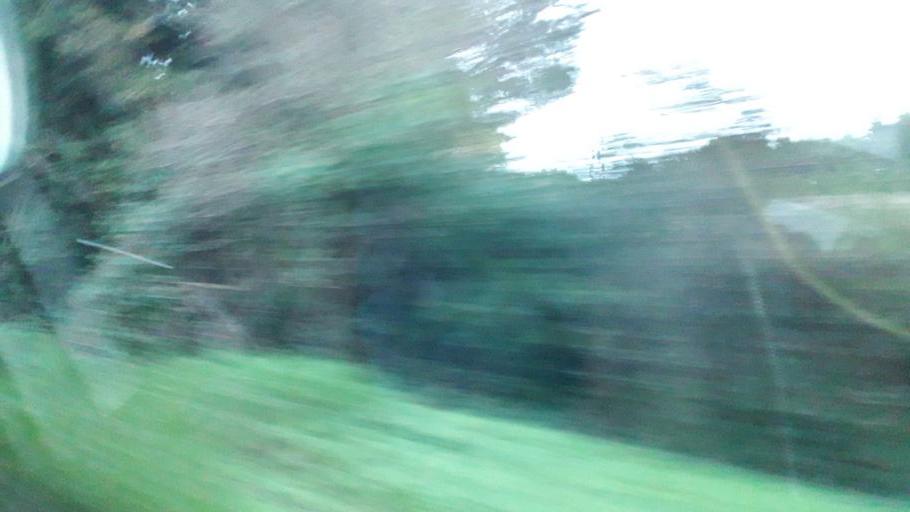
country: IE
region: Leinster
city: Malahide
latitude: 53.4376
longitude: -6.1770
